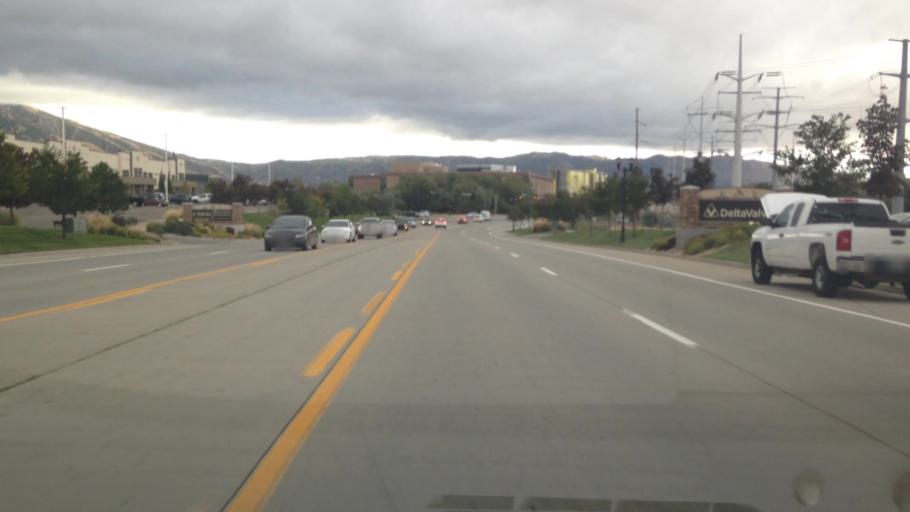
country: US
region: Utah
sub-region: Salt Lake County
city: South Jordan
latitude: 40.5717
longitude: -111.9056
